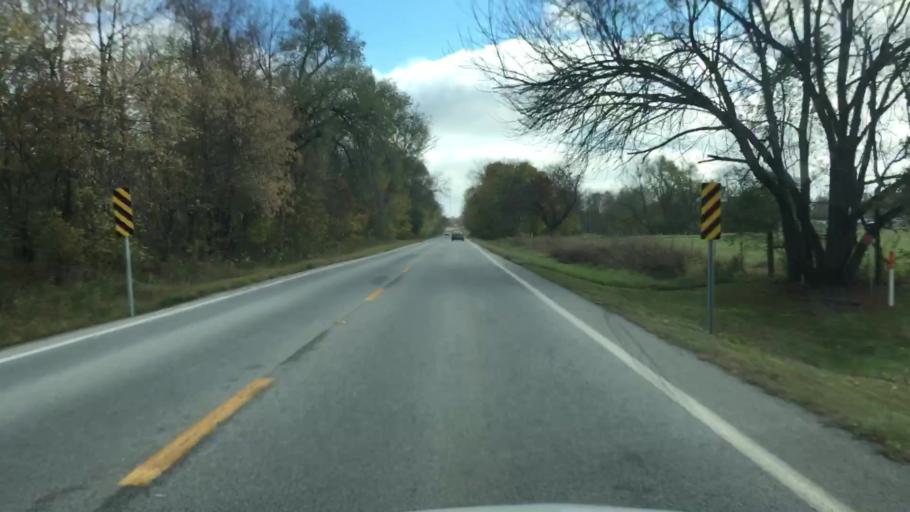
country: US
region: Arkansas
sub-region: Benton County
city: Gentry
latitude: 36.2601
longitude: -94.4145
